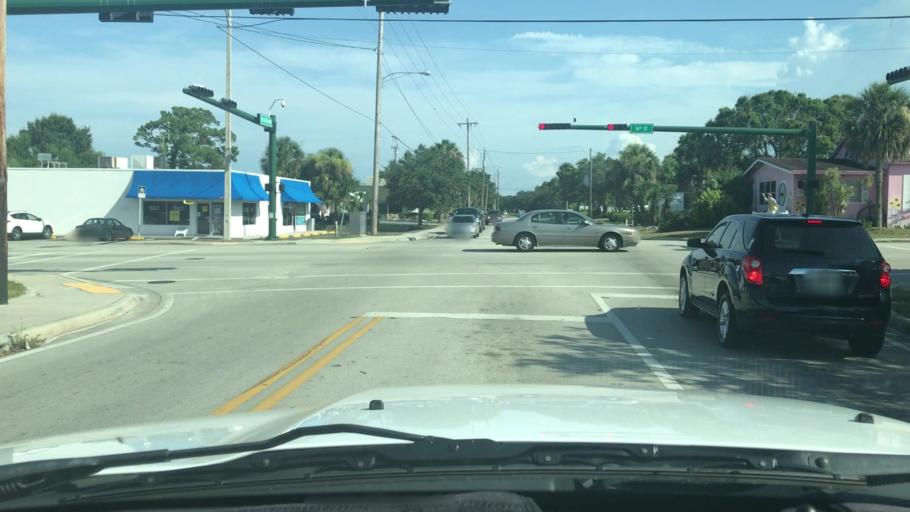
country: US
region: Florida
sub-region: Indian River County
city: Vero Beach
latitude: 27.6319
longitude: -80.3970
